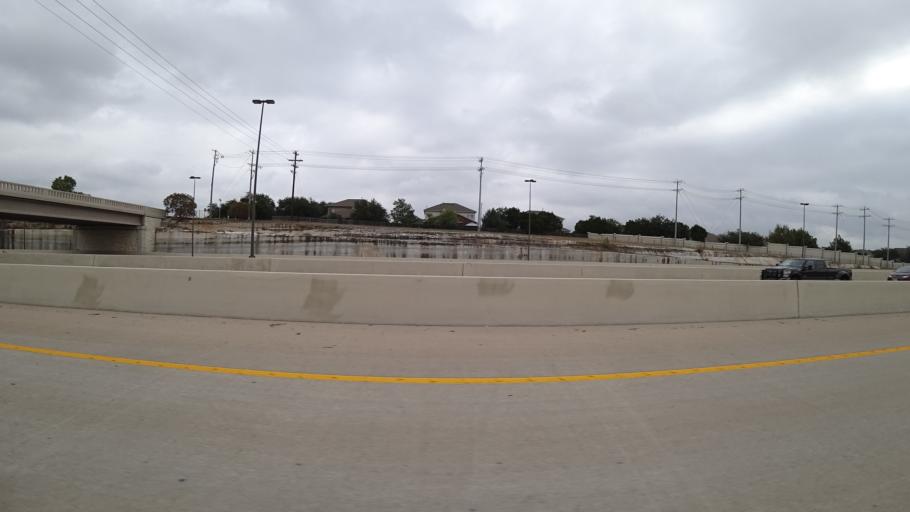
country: US
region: Texas
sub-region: Williamson County
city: Cedar Park
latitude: 30.5133
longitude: -97.8129
